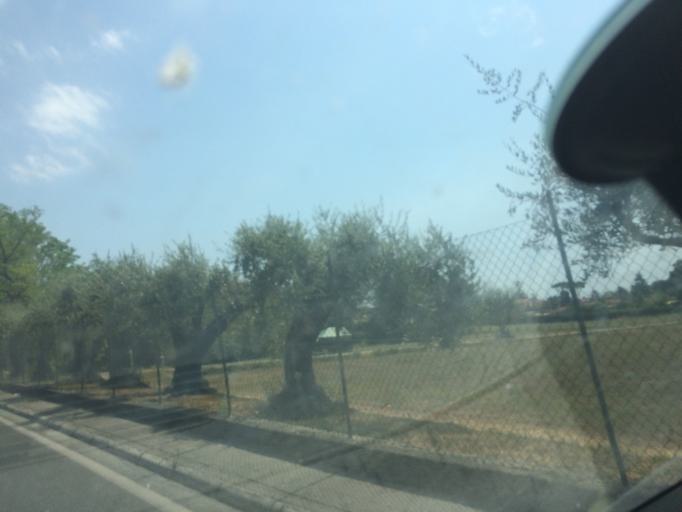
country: IT
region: Tuscany
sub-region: Provincia di Massa-Carrara
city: Carrara
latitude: 44.0466
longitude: 10.0568
